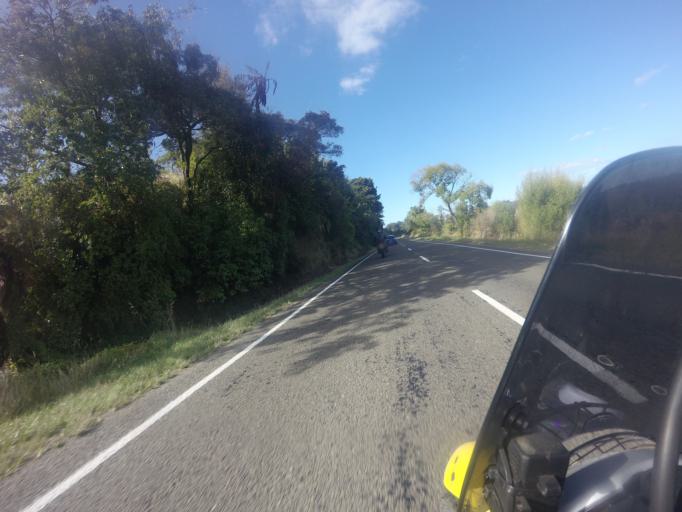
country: NZ
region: Bay of Plenty
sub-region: Opotiki District
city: Opotiki
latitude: -38.0236
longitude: 177.1775
